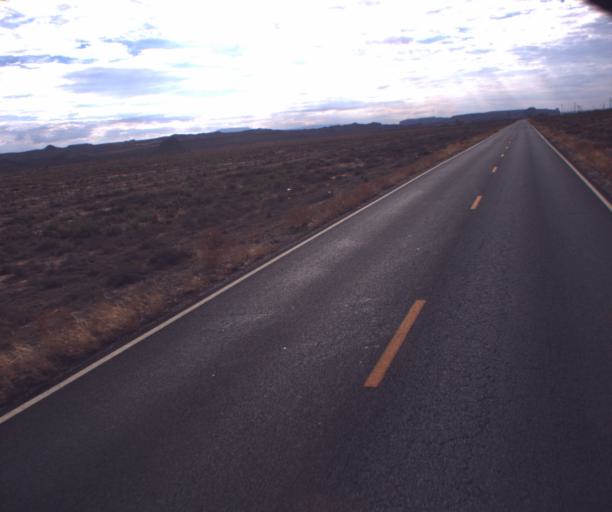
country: US
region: Arizona
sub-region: Apache County
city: Many Farms
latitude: 36.7443
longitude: -109.6392
